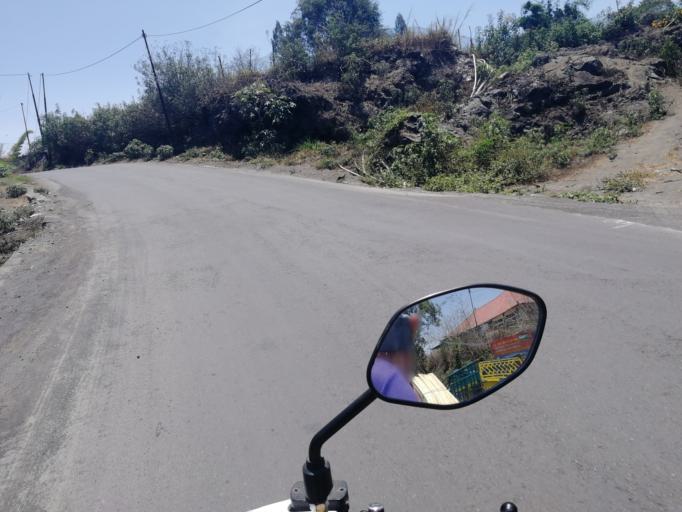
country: ID
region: Bali
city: Banjar Trunyan
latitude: -8.2301
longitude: 115.4083
